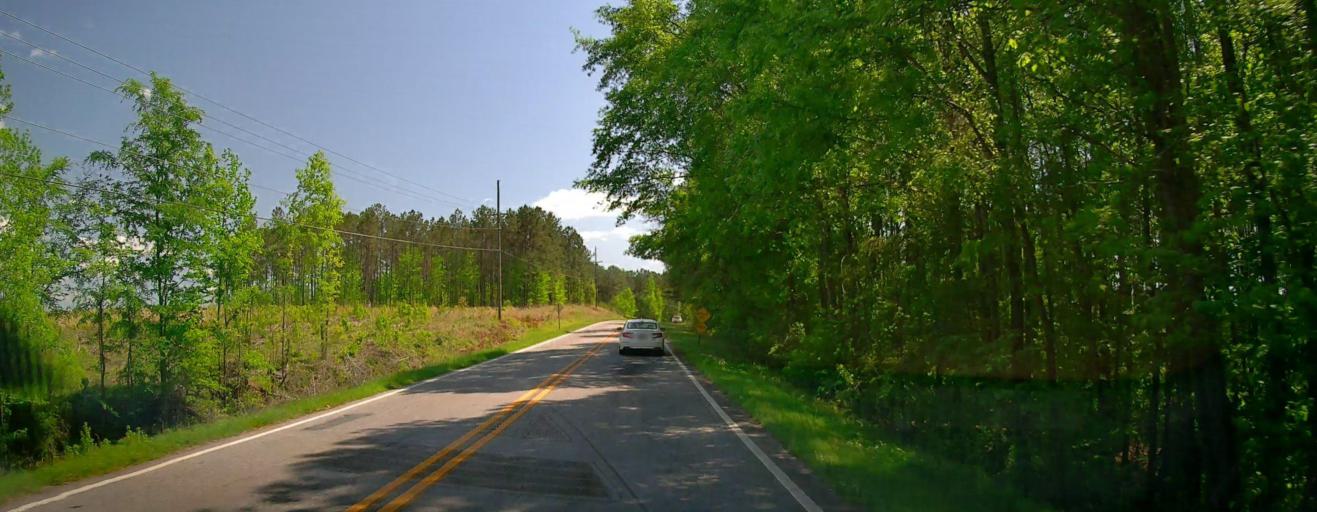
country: US
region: Georgia
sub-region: Putnam County
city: Eatonton
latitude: 33.2488
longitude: -83.3035
